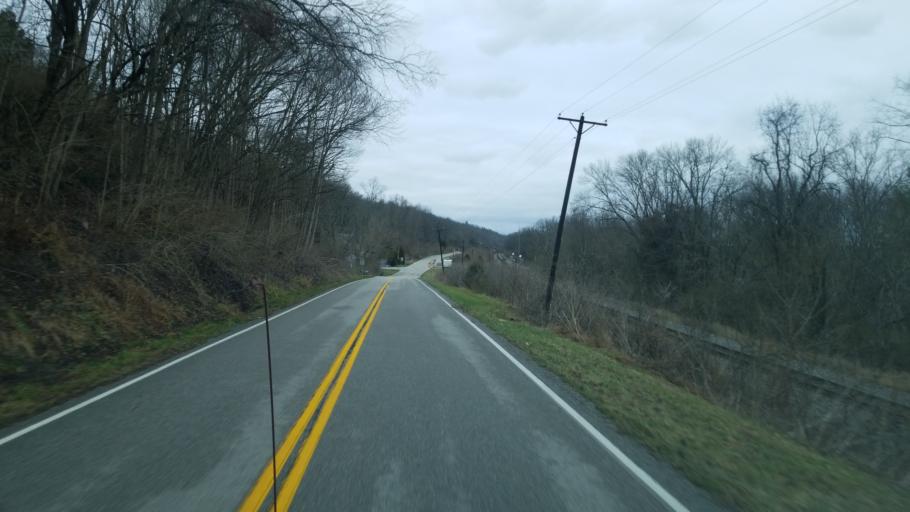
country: US
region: Ohio
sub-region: Clermont County
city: New Richmond
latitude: 38.9433
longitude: -84.2878
